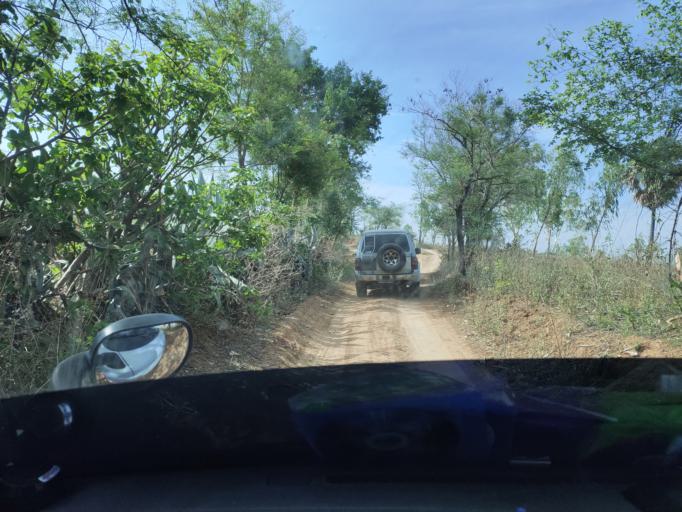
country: MM
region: Magway
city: Chauk
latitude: 20.9546
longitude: 94.9927
